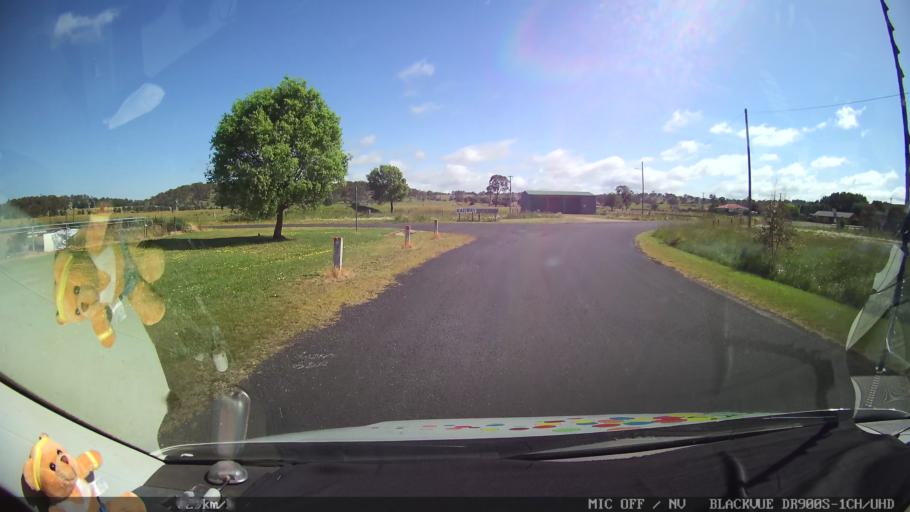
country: AU
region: New South Wales
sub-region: Guyra
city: Guyra
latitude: -30.1293
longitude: 151.6834
